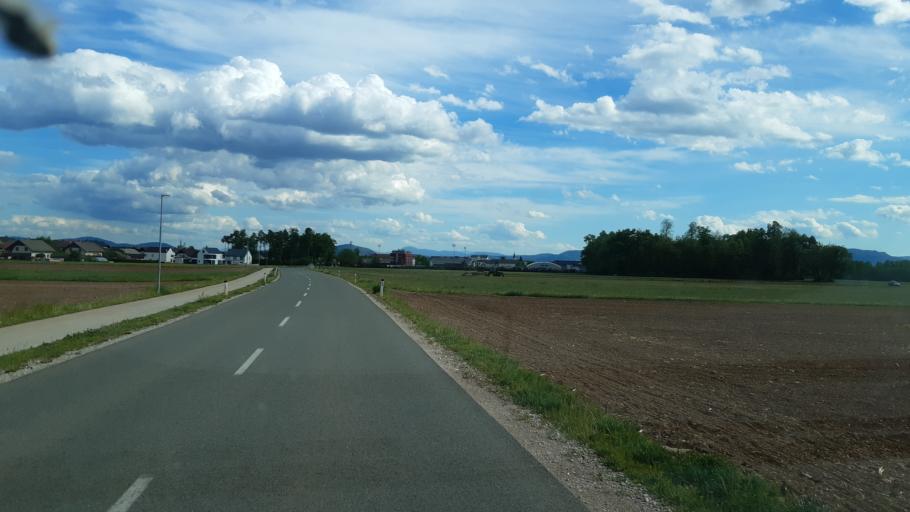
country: SI
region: Sencur
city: Sencur
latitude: 46.2556
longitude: 14.4189
